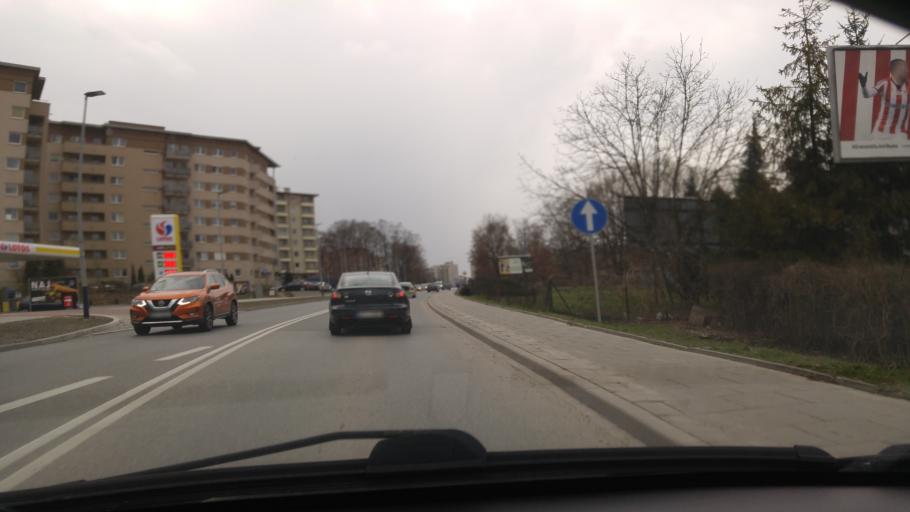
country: PL
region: Lesser Poland Voivodeship
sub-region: Powiat krakowski
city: Michalowice
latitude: 50.0934
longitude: 20.0268
